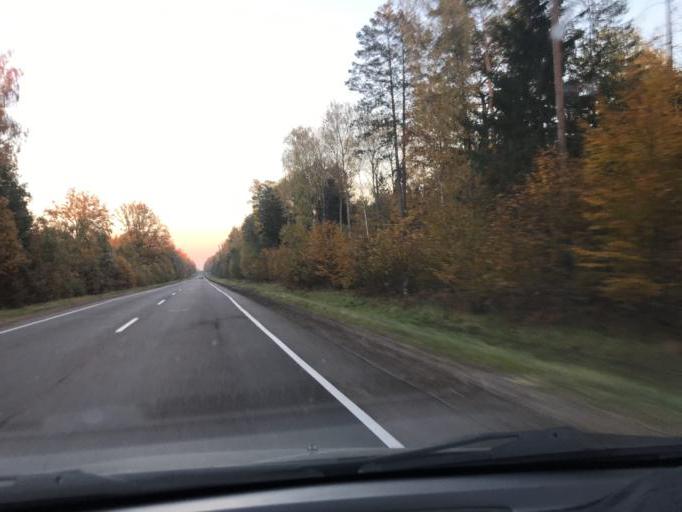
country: BY
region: Mogilev
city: Hlusha
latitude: 53.0898
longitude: 28.8925
